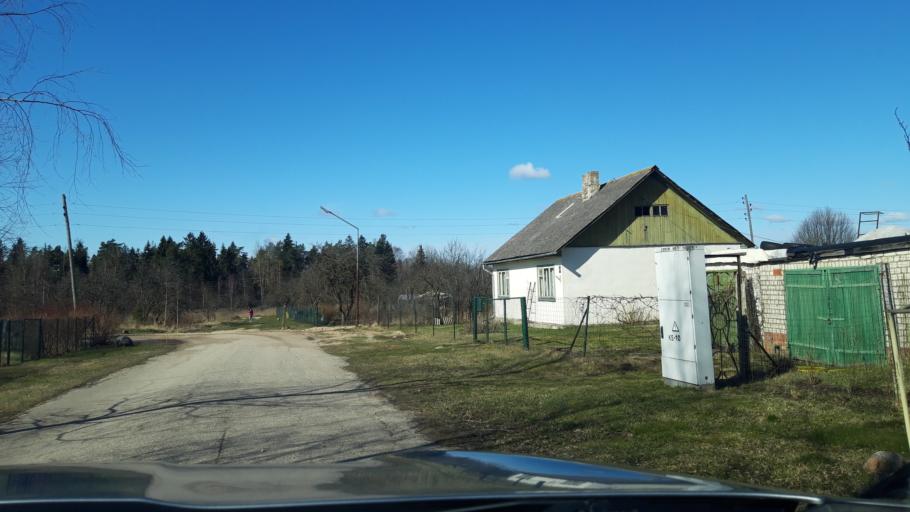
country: LV
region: Strenci
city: Seda
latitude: 57.6527
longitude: 25.7503
